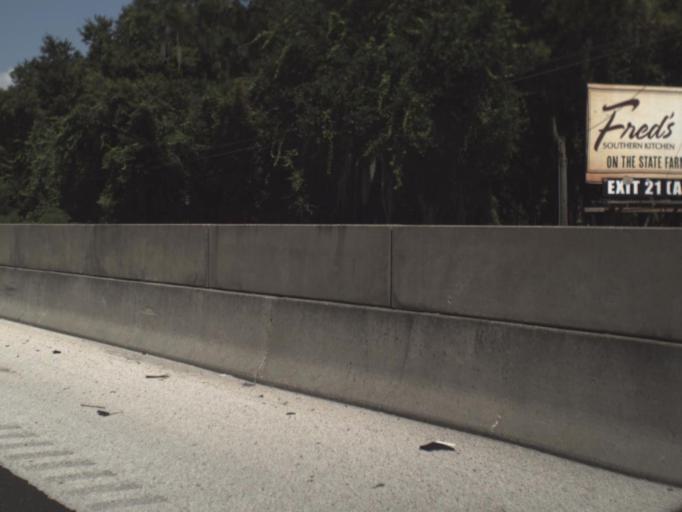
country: US
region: Florida
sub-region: Hillsborough County
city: Plant City
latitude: 28.0370
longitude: -82.0927
